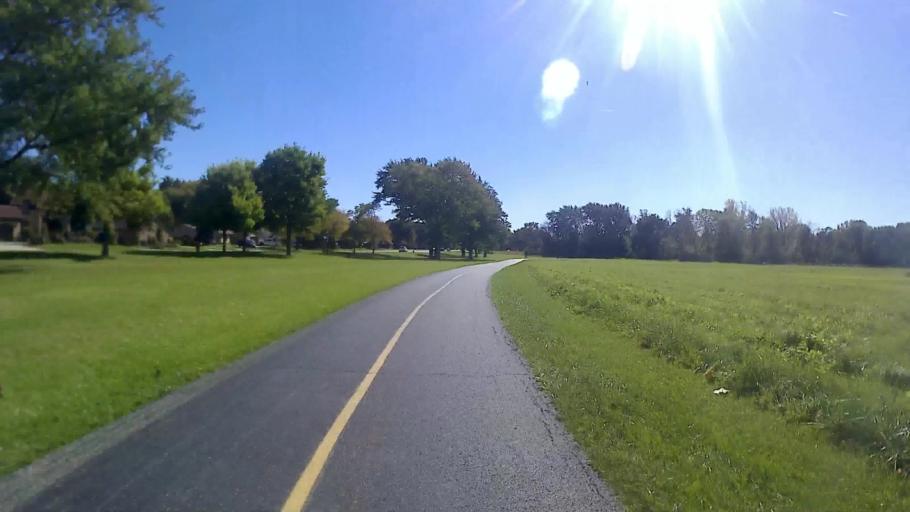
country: US
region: Illinois
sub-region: Cook County
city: Elk Grove Village
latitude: 42.0253
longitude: -87.9889
